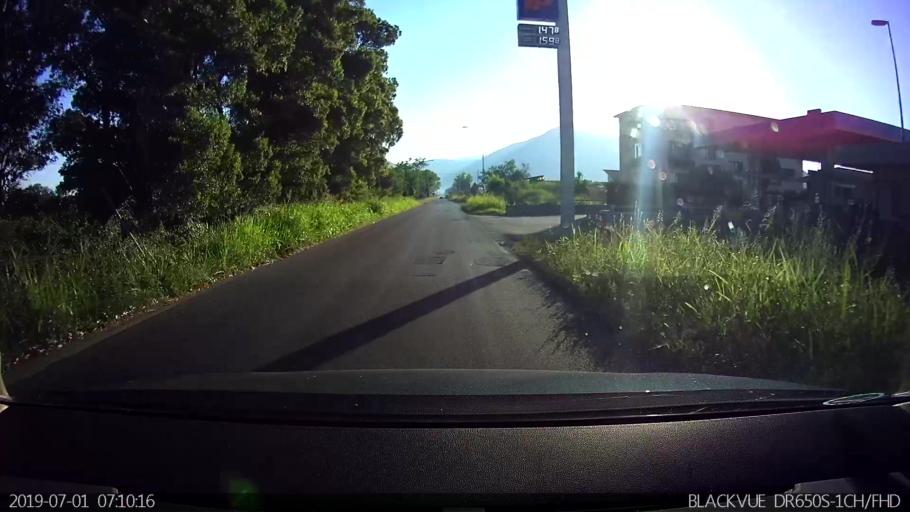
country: IT
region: Latium
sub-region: Provincia di Latina
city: Borgo Hermada
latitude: 41.3110
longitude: 13.1688
